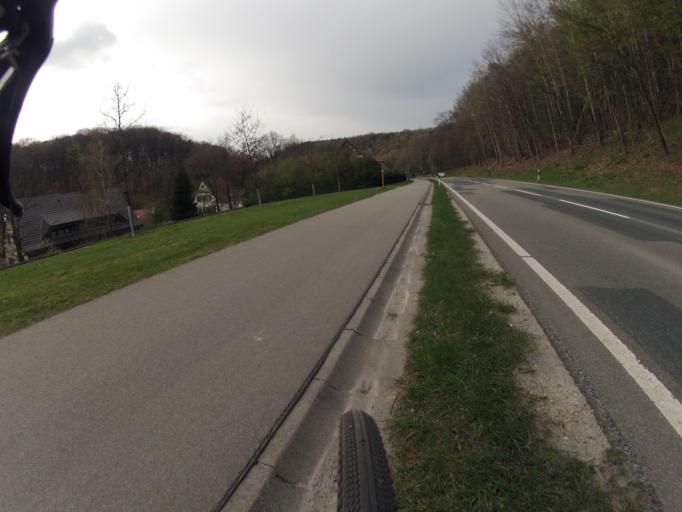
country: DE
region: North Rhine-Westphalia
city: Ibbenburen
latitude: 52.2321
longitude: 7.7506
